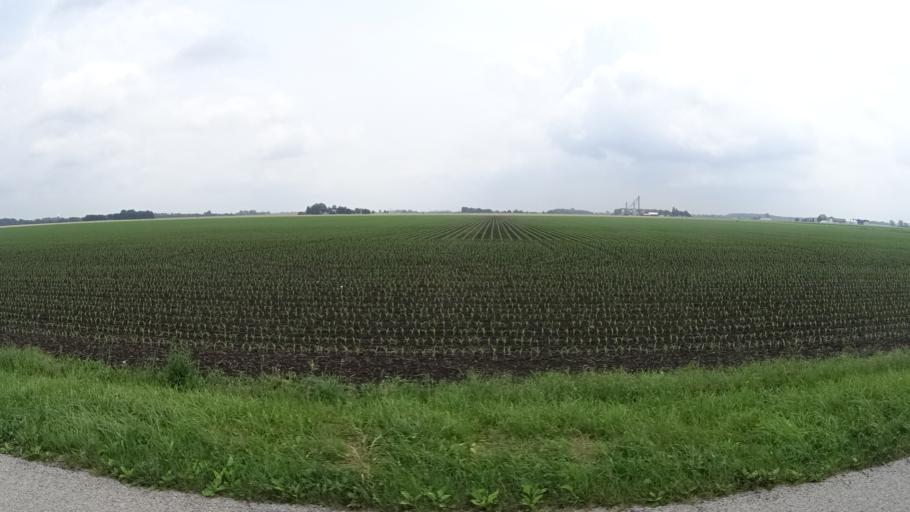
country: US
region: Ohio
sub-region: Huron County
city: Bellevue
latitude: 41.3075
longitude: -82.8049
